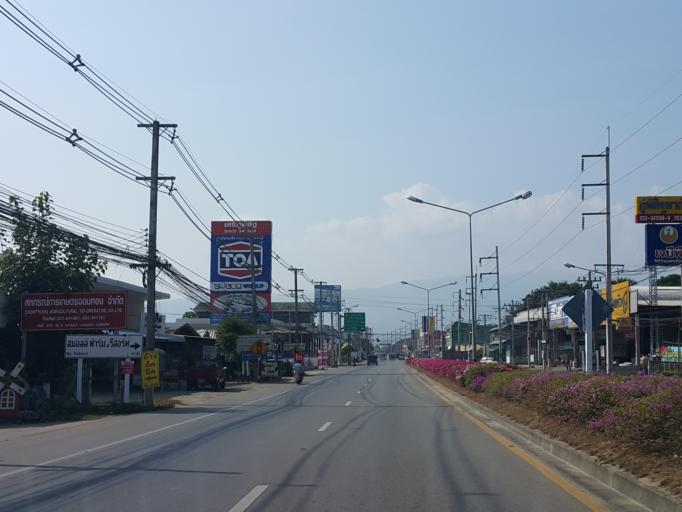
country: TH
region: Chiang Mai
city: Chom Thong
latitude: 18.4348
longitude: 98.6860
